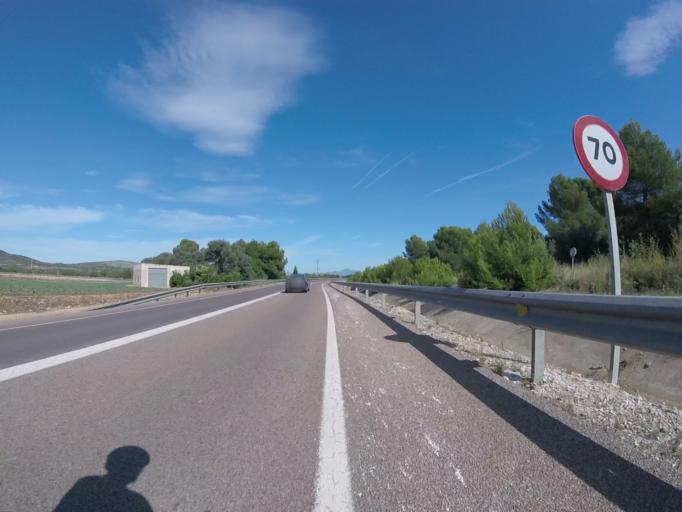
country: ES
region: Valencia
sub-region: Provincia de Castello
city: Peniscola
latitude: 40.3940
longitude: 0.3608
